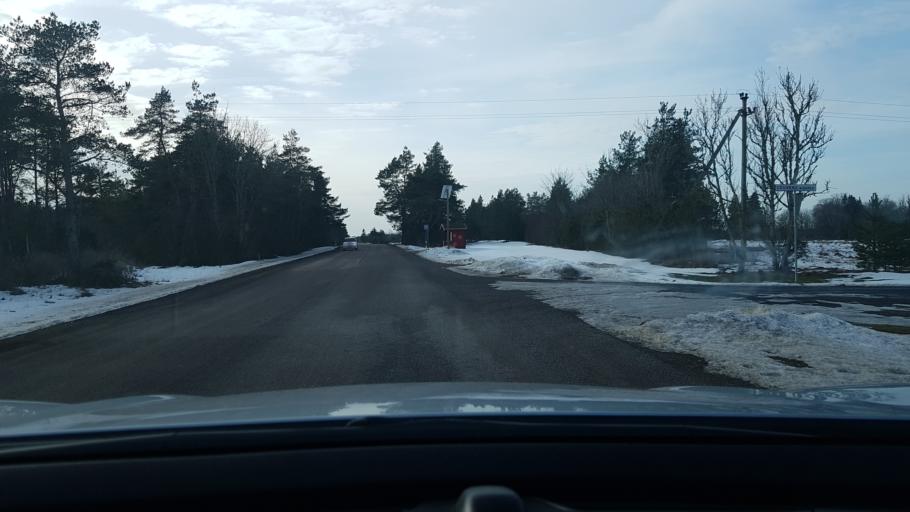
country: EE
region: Saare
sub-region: Kuressaare linn
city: Kuressaare
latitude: 58.3386
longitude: 22.5727
